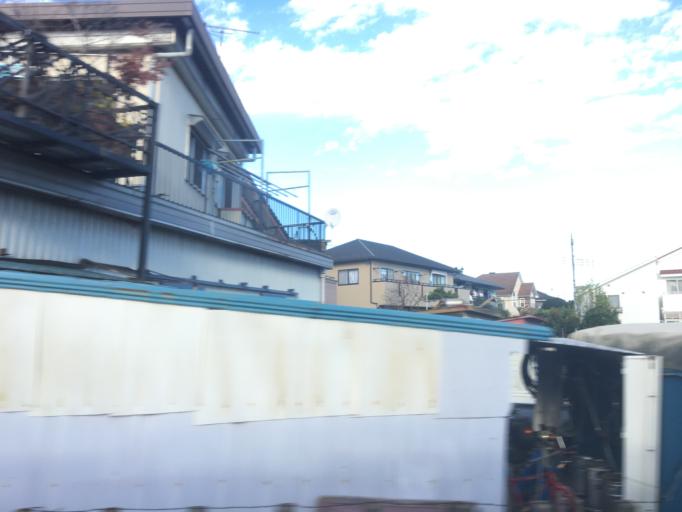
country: JP
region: Saitama
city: Shiki
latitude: 35.8372
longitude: 139.5527
